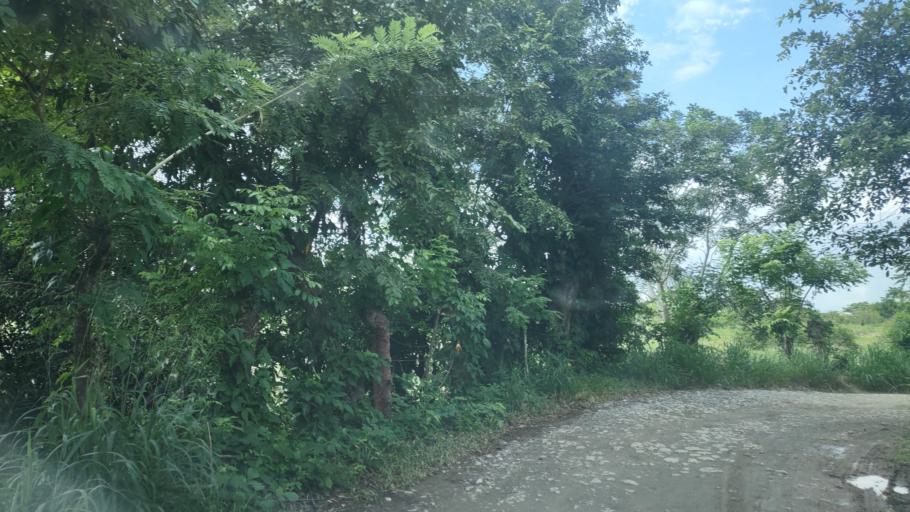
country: MX
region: Veracruz
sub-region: Atzalan
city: Colonias Pedernales
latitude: 20.0563
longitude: -97.0137
